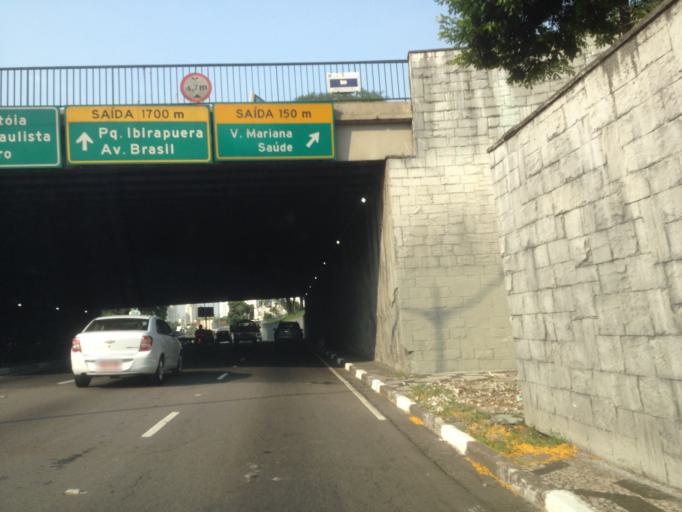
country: BR
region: Sao Paulo
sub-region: Sao Paulo
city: Sao Paulo
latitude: -23.6082
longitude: -46.6530
